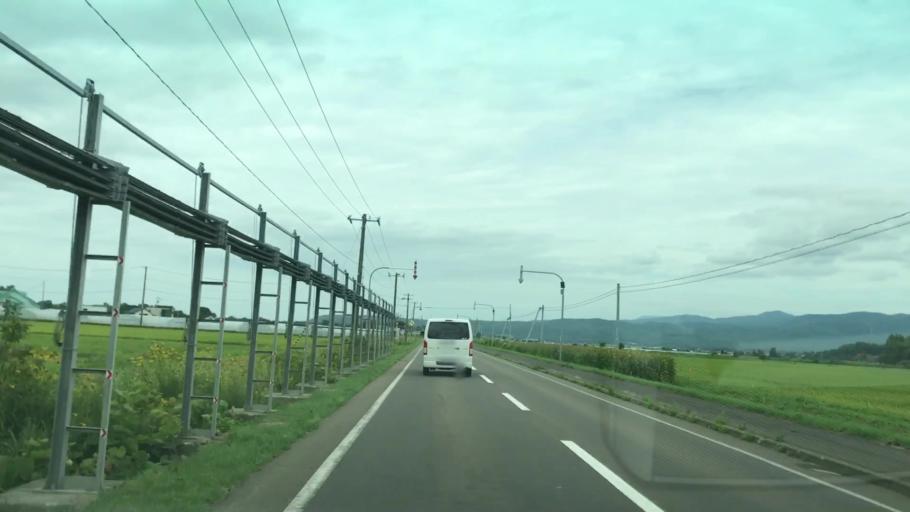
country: JP
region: Hokkaido
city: Iwanai
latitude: 42.9980
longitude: 140.5933
